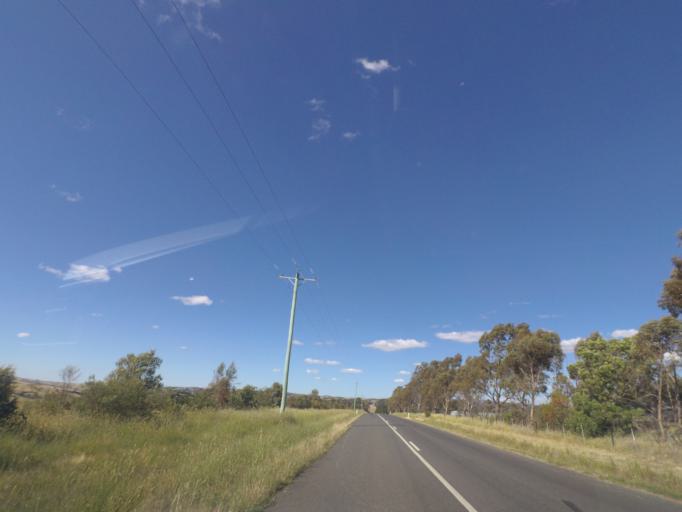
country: AU
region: Victoria
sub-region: Hume
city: Craigieburn
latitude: -37.4114
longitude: 144.8904
